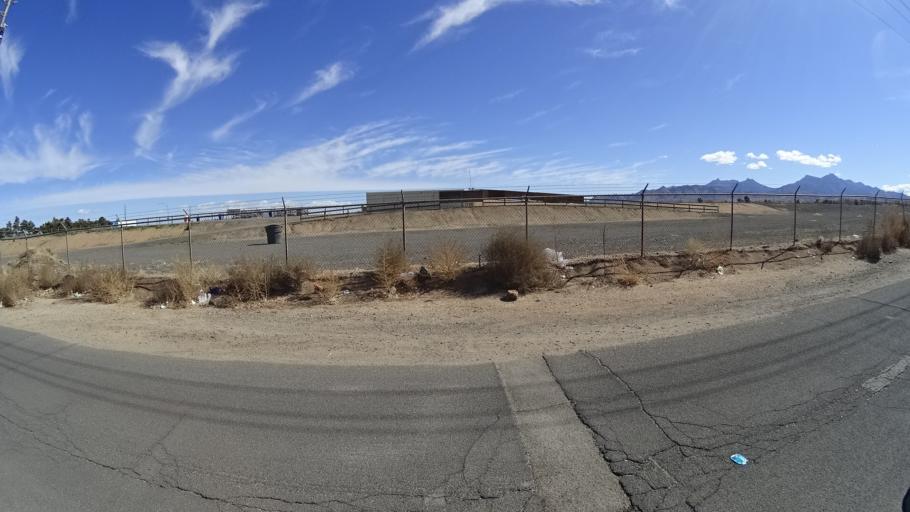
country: US
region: Arizona
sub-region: Mohave County
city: Kingman
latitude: 35.2159
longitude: -114.0293
